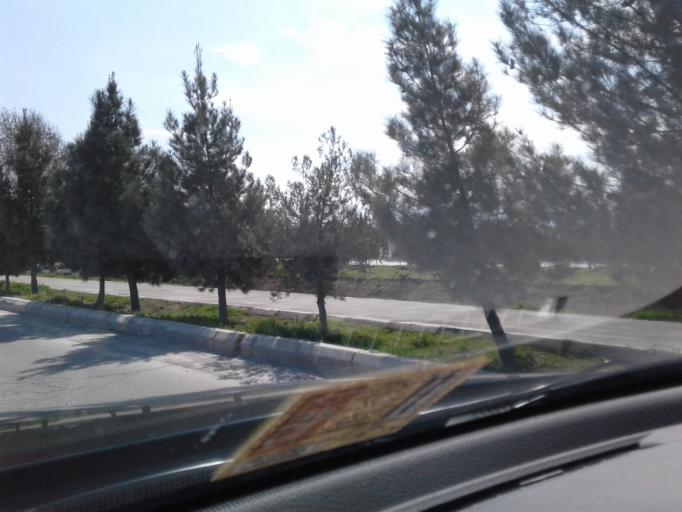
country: TM
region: Ahal
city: Abadan
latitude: 38.0653
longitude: 58.2547
